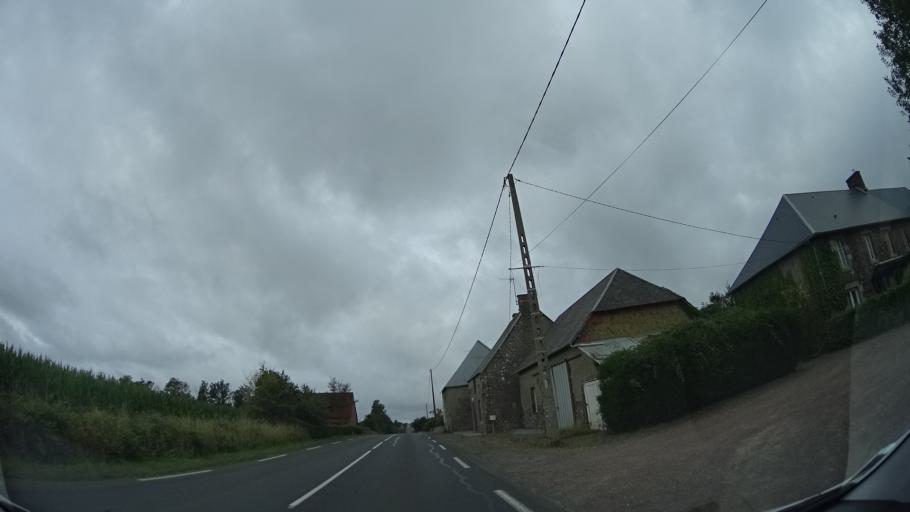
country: FR
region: Lower Normandy
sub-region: Departement de la Manche
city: Gavray
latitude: 48.9258
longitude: -1.3698
